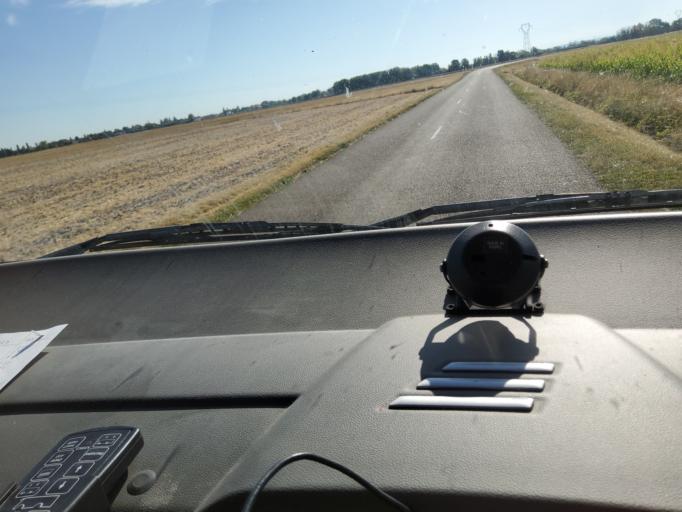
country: FR
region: Bourgogne
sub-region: Departement de la Cote-d'Or
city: Saint-Usage
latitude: 47.1398
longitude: 5.2597
